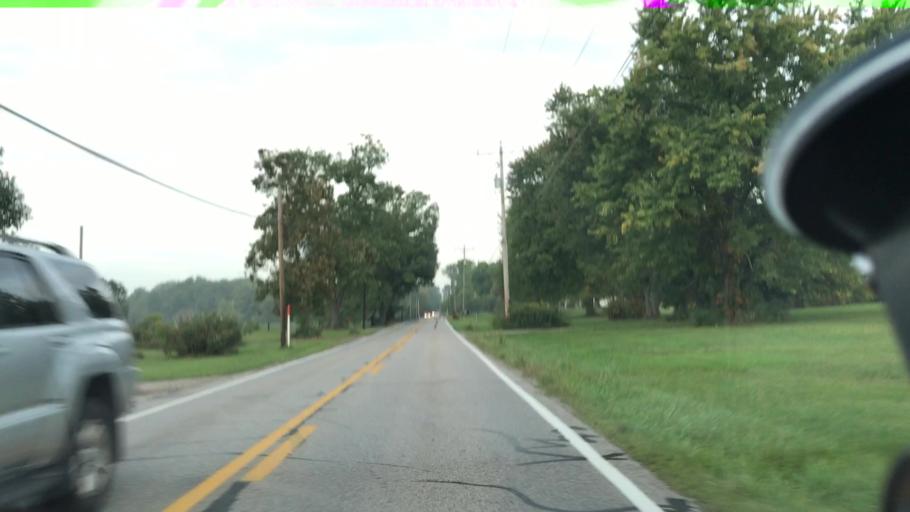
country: US
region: Ohio
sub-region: Delaware County
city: Lewis Center
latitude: 40.1753
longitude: -83.0251
